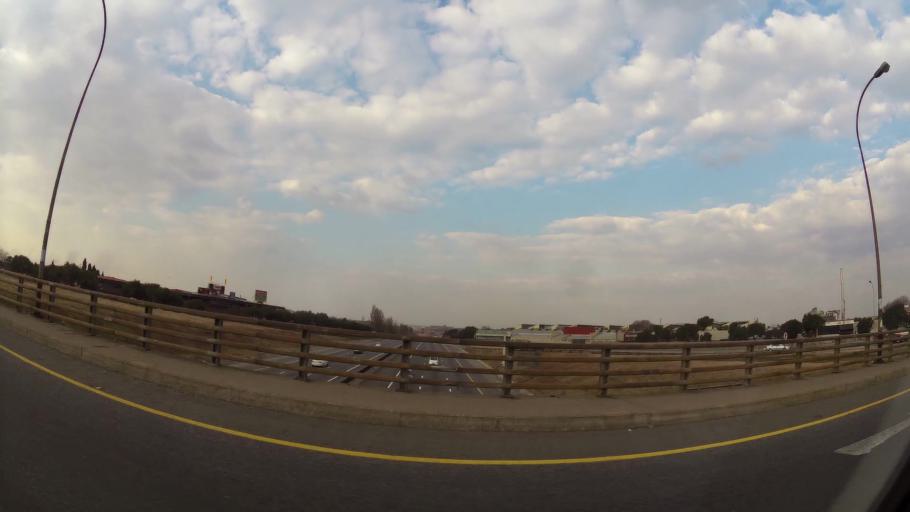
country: ZA
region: Gauteng
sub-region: Ekurhuleni Metropolitan Municipality
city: Germiston
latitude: -26.2558
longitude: 28.1889
